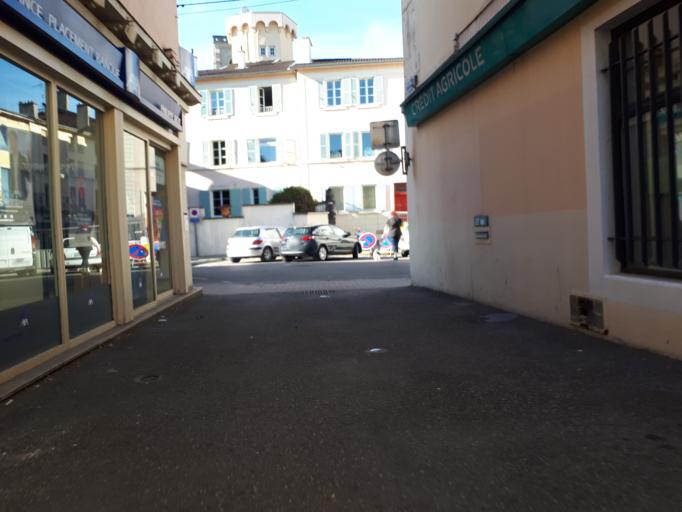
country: FR
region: Rhone-Alpes
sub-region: Departement de l'Isere
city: Bourgoin-Jallieu
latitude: 45.5851
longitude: 5.2765
